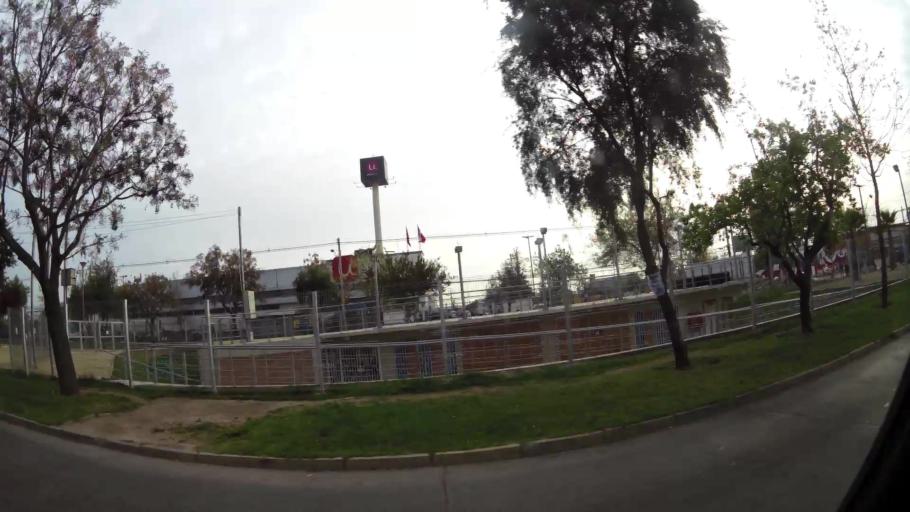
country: CL
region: Santiago Metropolitan
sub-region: Provincia de Maipo
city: San Bernardo
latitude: -33.5317
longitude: -70.7742
